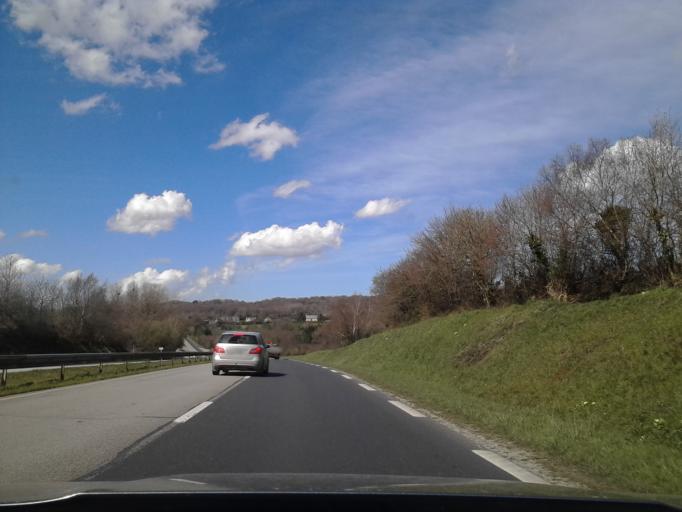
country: FR
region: Lower Normandy
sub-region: Departement de la Manche
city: Brix
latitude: 49.5375
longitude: -1.5379
